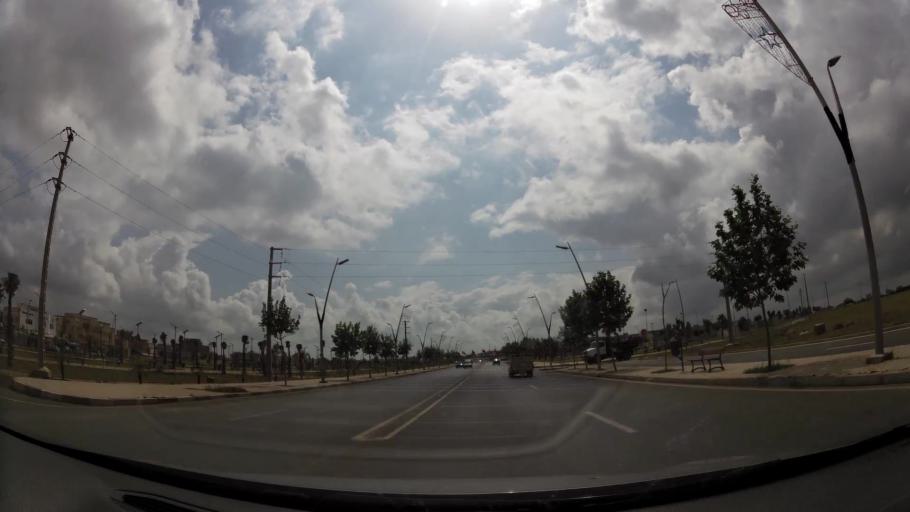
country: MA
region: Rabat-Sale-Zemmour-Zaer
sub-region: Khemisset
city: Tiflet
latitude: 33.8945
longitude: -6.3369
